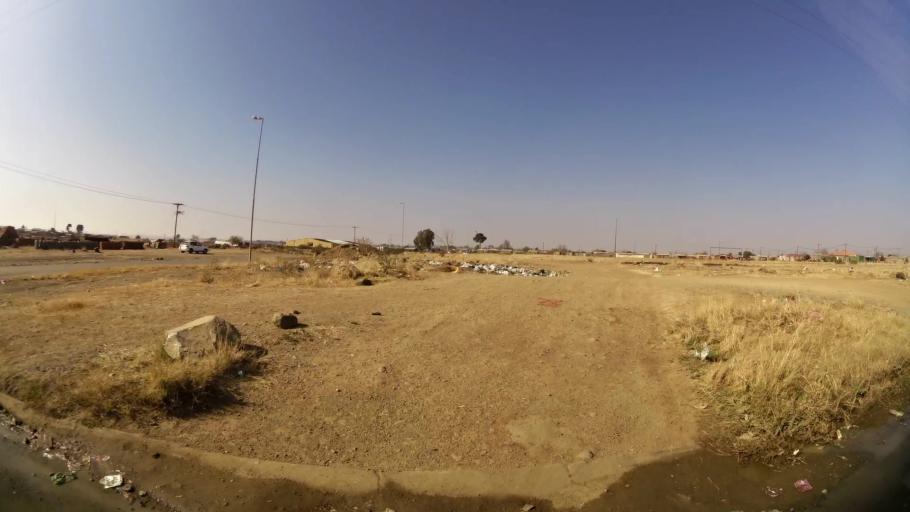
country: ZA
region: Orange Free State
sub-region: Mangaung Metropolitan Municipality
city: Bloemfontein
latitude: -29.1957
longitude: 26.2603
